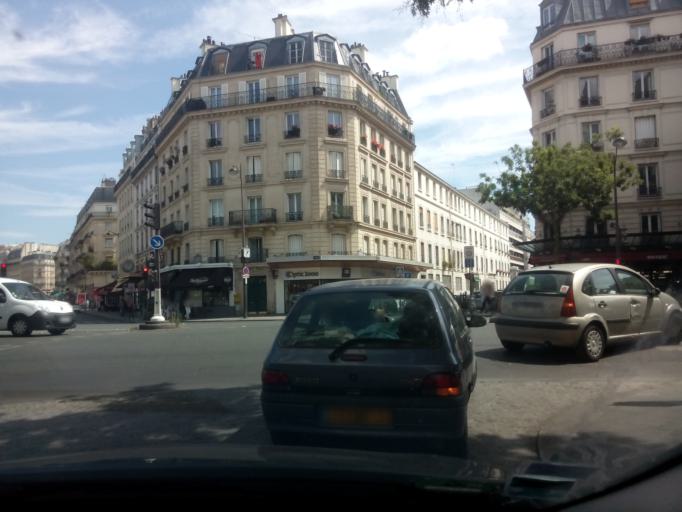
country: FR
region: Ile-de-France
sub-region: Paris
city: Paris
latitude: 48.8384
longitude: 2.3507
